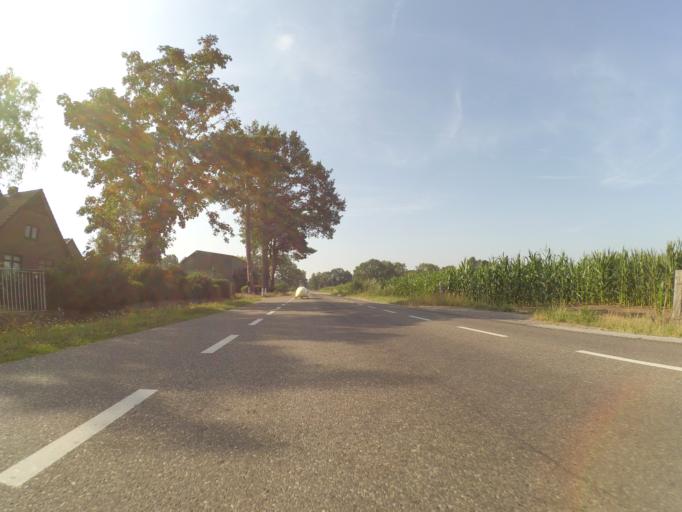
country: NL
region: Overijssel
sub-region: Gemeente Tubbergen
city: Tubbergen
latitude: 52.3783
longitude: 6.8515
